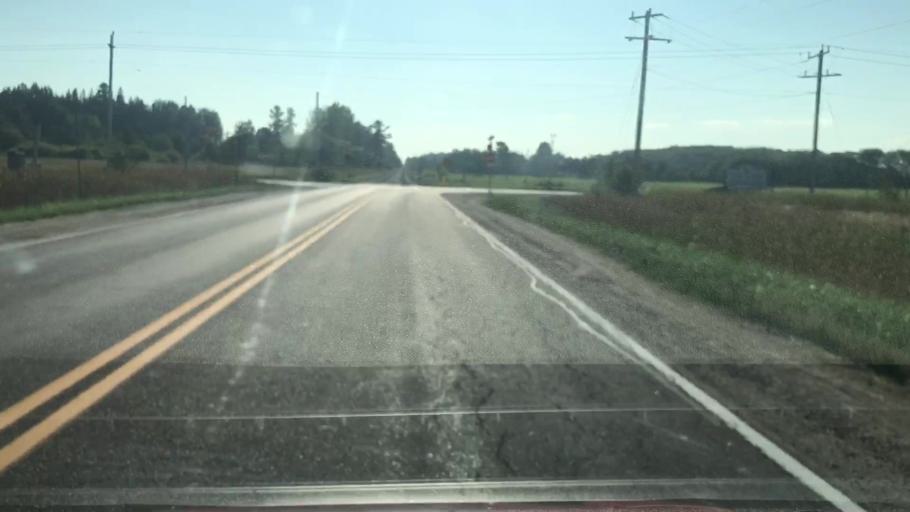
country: US
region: Michigan
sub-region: Chippewa County
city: Sault Ste. Marie
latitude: 46.2763
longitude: -84.0270
